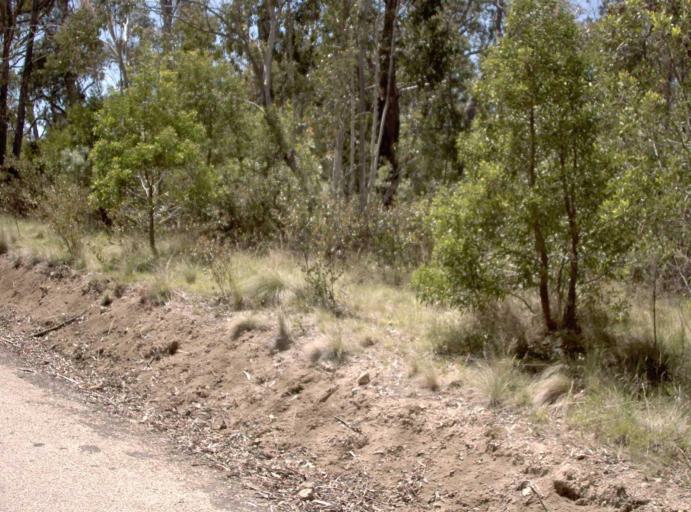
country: AU
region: Victoria
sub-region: East Gippsland
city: Lakes Entrance
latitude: -37.1266
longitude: 148.2455
